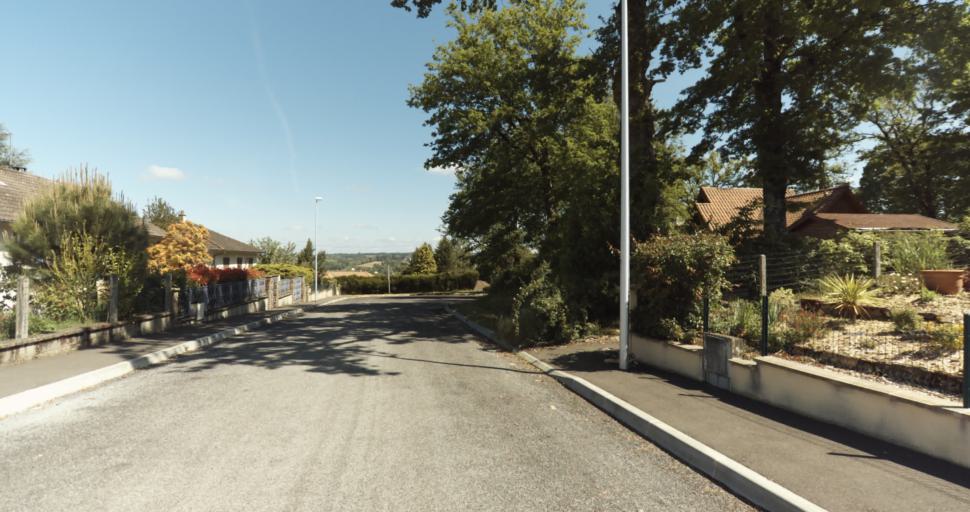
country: FR
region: Limousin
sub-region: Departement de la Haute-Vienne
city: Le Vigen
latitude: 45.7397
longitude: 1.2871
